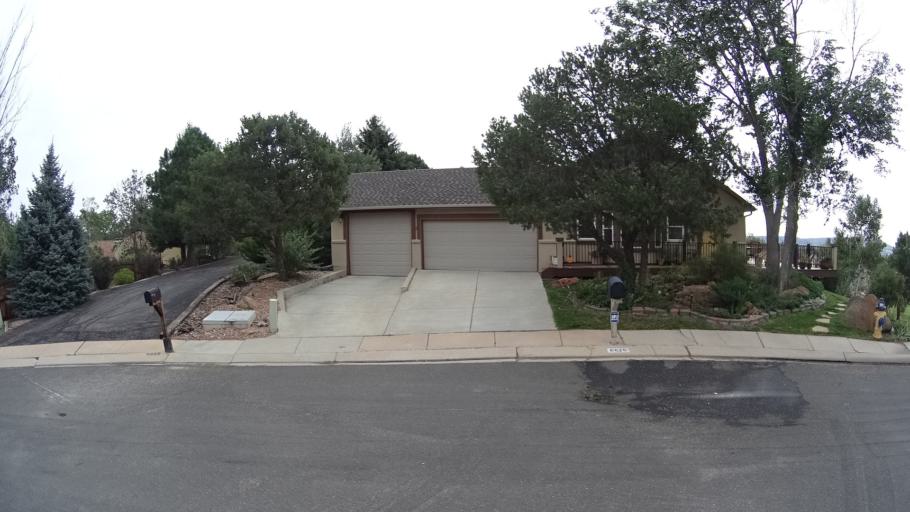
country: US
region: Colorado
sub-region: El Paso County
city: Air Force Academy
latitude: 38.9280
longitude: -104.8427
